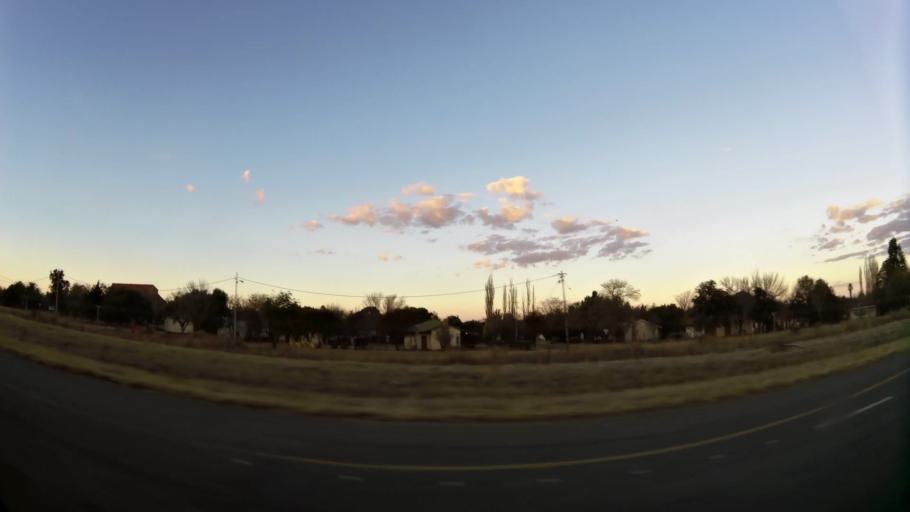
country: ZA
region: North-West
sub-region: Dr Kenneth Kaunda District Municipality
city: Potchefstroom
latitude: -26.6813
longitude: 27.0755
